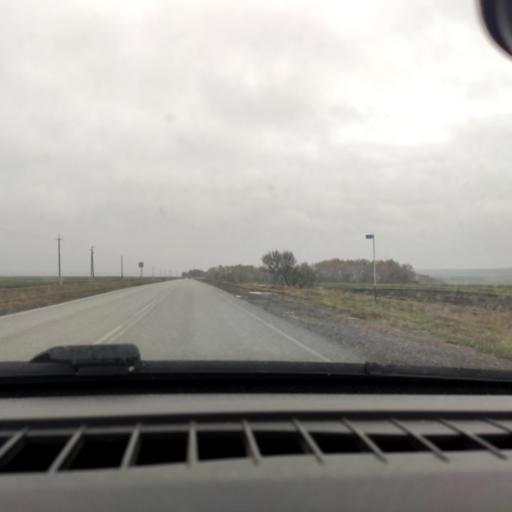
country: RU
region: Belgorod
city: Ilovka
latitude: 50.7527
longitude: 38.7190
